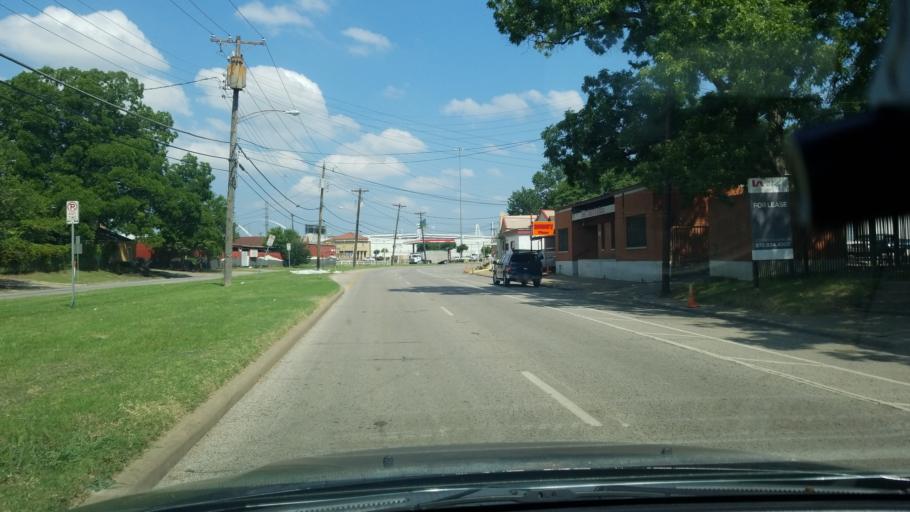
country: US
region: Texas
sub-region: Dallas County
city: Dallas
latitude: 32.7641
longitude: -96.8013
